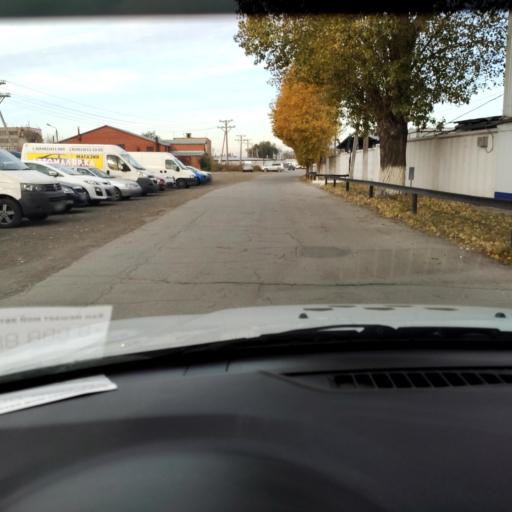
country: RU
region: Samara
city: Tol'yatti
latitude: 53.5696
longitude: 49.4646
